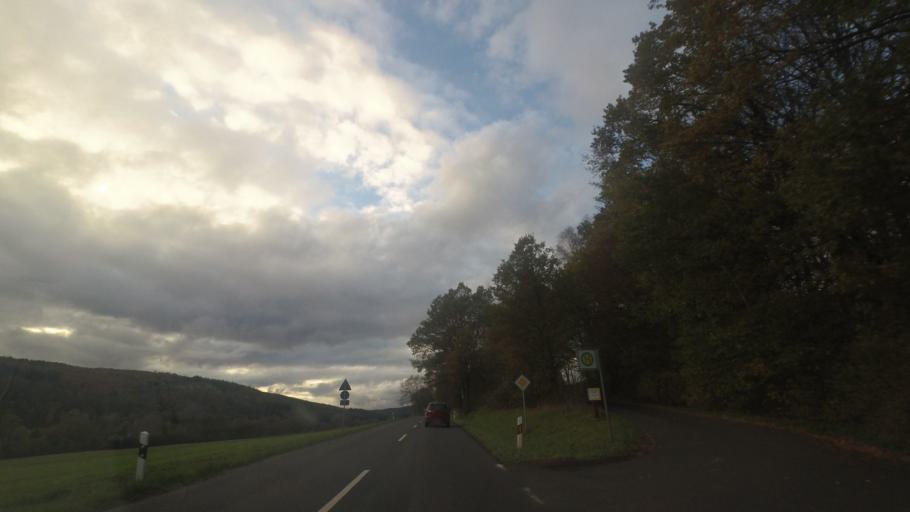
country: DE
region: Hesse
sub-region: Regierungsbezirk Kassel
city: Flieden
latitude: 50.4546
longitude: 9.5570
